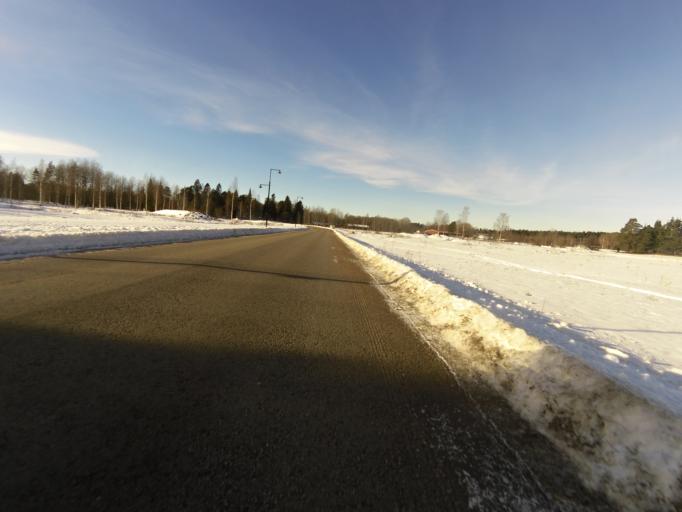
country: SE
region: Gaevleborg
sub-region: Gavle Kommun
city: Gavle
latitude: 60.6624
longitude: 17.0887
